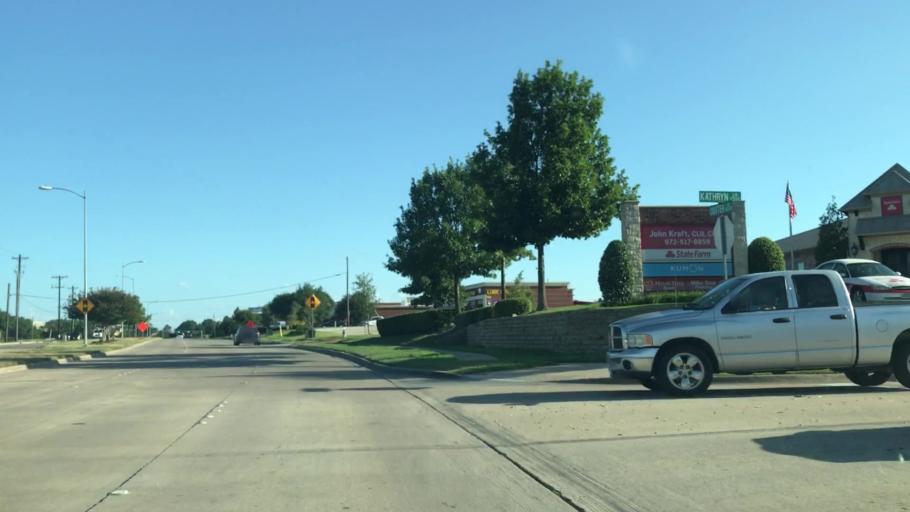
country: US
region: Texas
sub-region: Collin County
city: Allen
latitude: 33.1185
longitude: -96.7335
